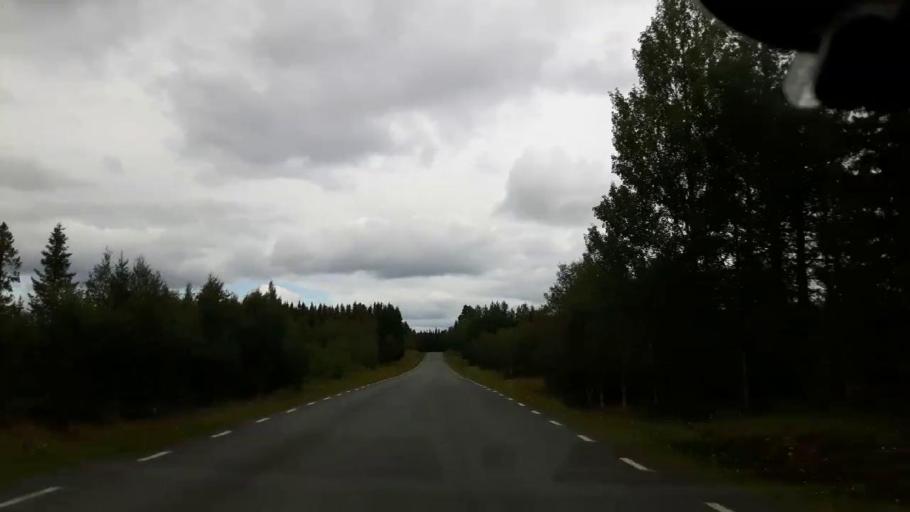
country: SE
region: Jaemtland
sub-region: Krokoms Kommun
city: Valla
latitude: 63.5527
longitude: 13.8502
